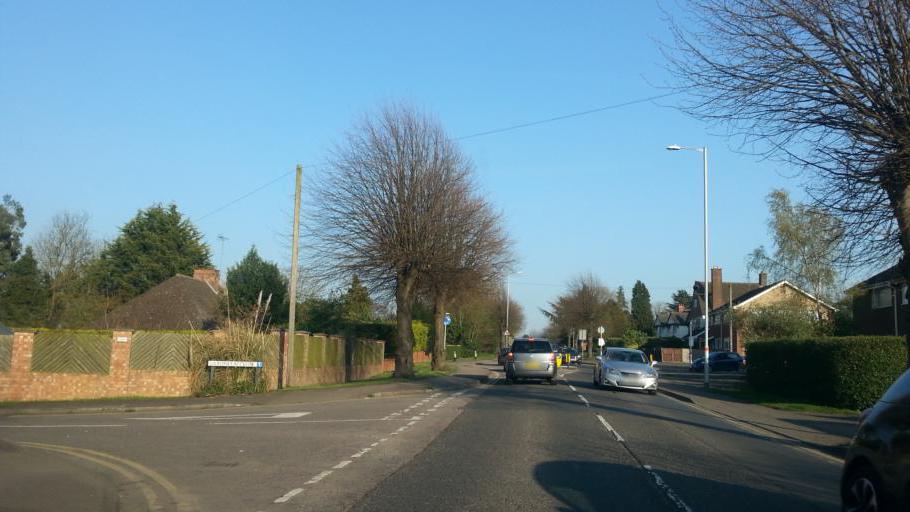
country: GB
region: England
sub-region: Northamptonshire
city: Rushden
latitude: 52.2954
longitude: -0.6197
